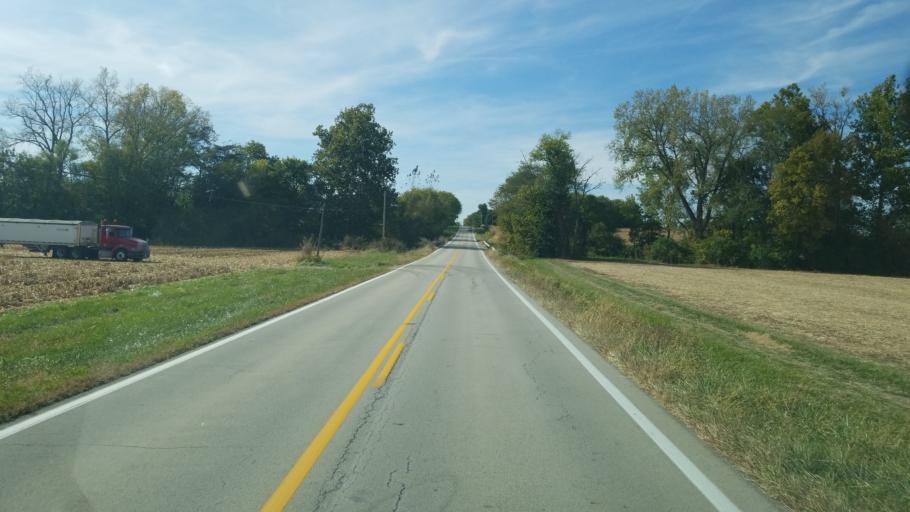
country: US
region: Ohio
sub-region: Clinton County
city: Wilmington
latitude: 39.3548
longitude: -83.7924
